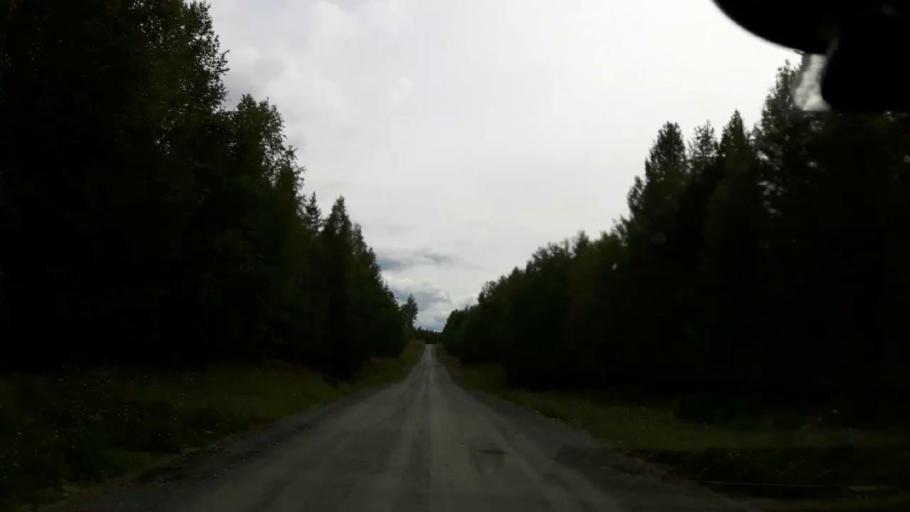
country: SE
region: Jaemtland
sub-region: Krokoms Kommun
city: Valla
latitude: 63.6551
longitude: 13.9788
